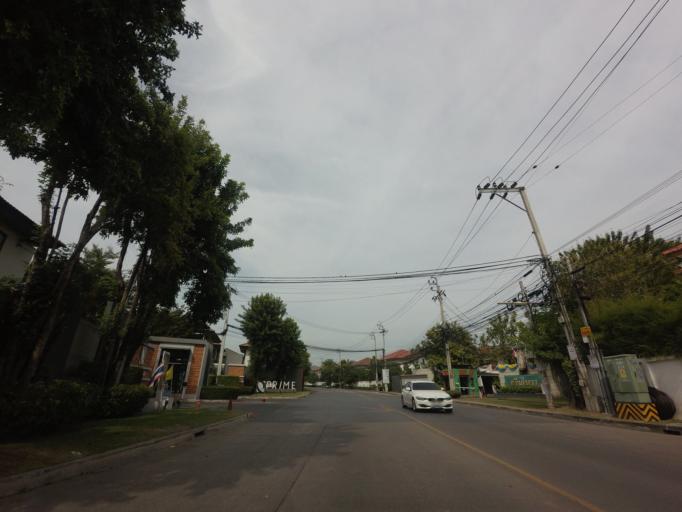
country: TH
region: Bangkok
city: Khlong Sam Wa
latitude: 13.8809
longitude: 100.7116
